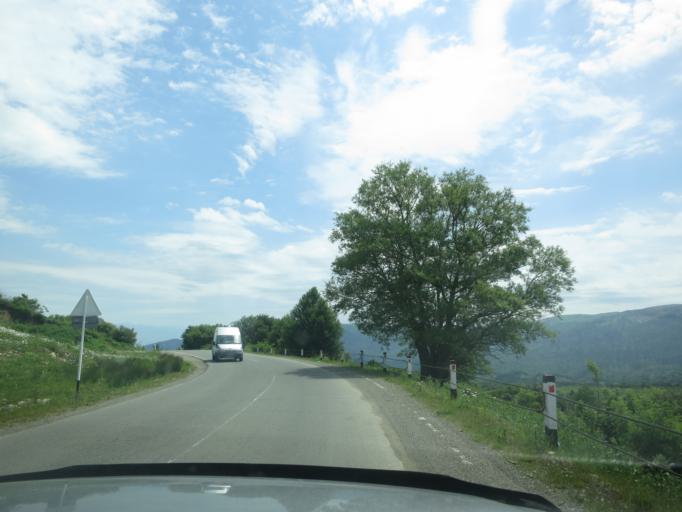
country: GE
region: Kakheti
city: Sagarejo
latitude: 41.8640
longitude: 45.2801
